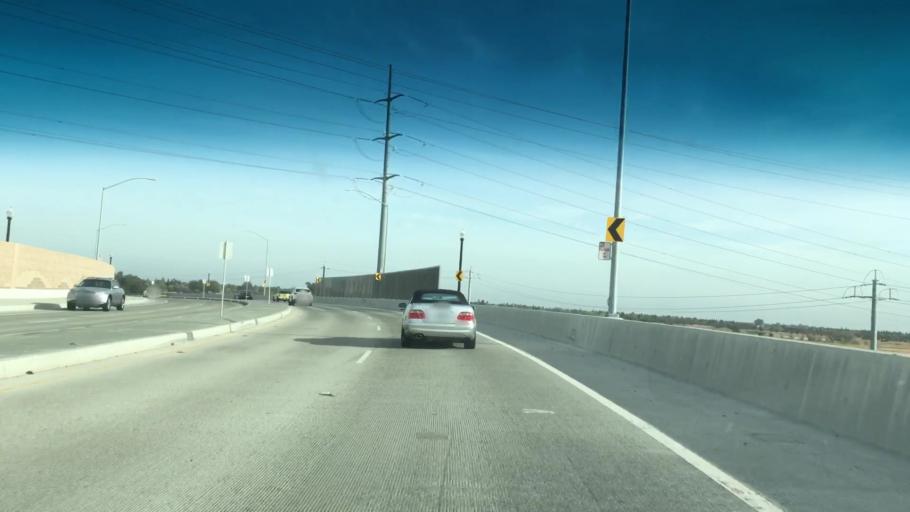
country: US
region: California
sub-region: Sacramento County
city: Parkway
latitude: 38.4608
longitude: -121.4616
